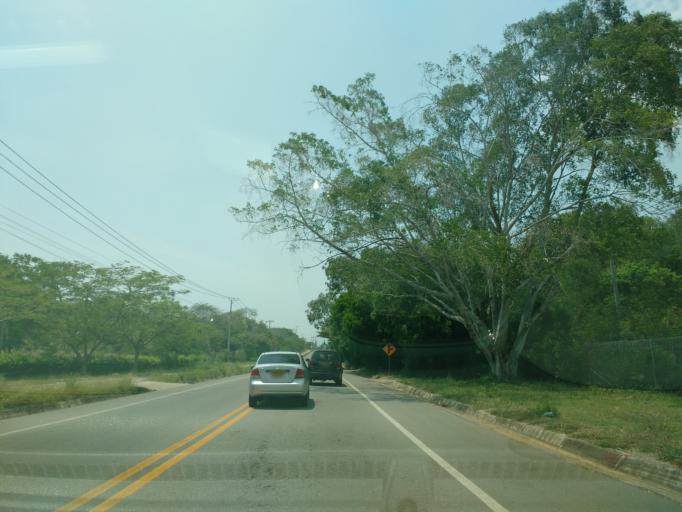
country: CO
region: Cundinamarca
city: Ricaurte
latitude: 4.2715
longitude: -74.7549
